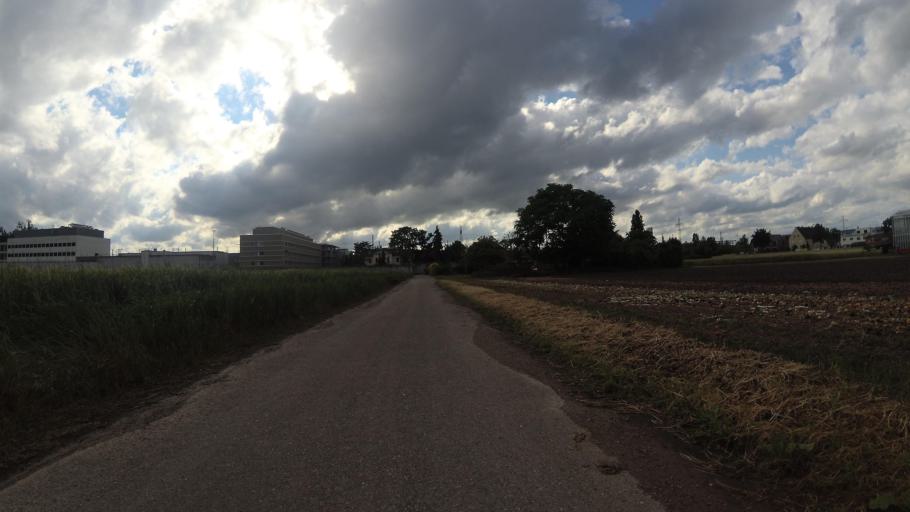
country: DE
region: Baden-Wuerttemberg
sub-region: Freiburg Region
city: Weil am Rhein
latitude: 47.5793
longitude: 7.6069
